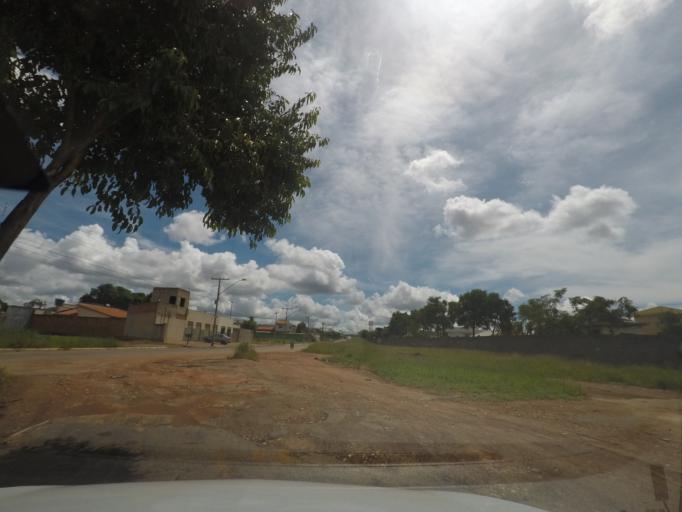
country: BR
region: Goias
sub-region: Goiania
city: Goiania
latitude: -16.7539
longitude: -49.3427
